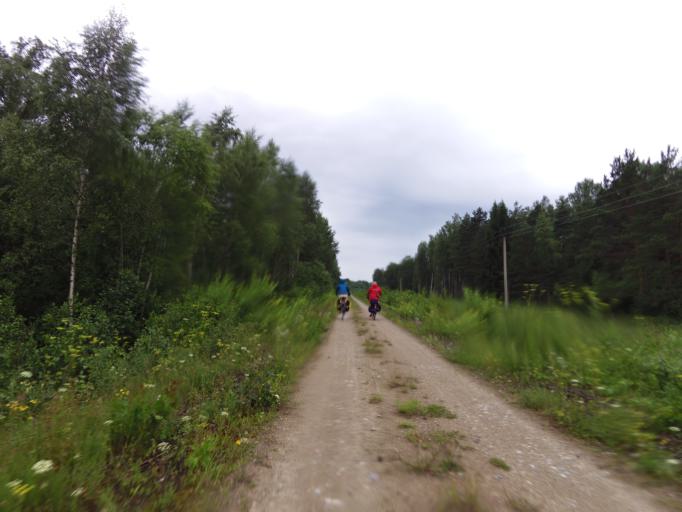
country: EE
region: Harju
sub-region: Nissi vald
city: Turba
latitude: 58.9892
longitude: 23.9905
